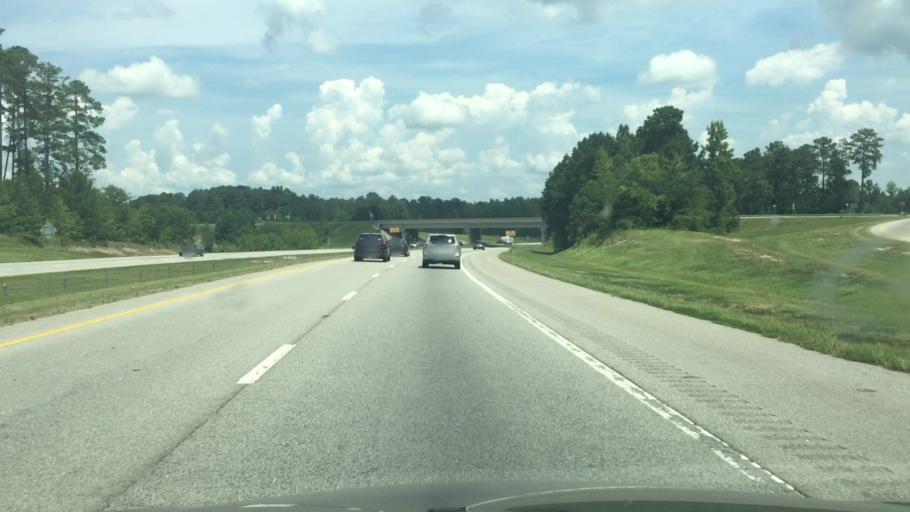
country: US
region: North Carolina
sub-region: Richmond County
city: Ellerbe
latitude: 35.0410
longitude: -79.7681
